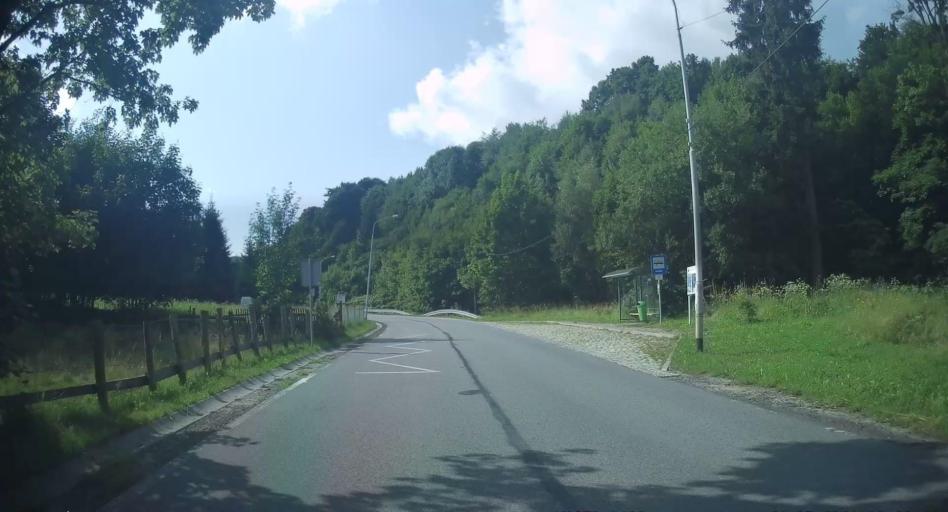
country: PL
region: Lower Silesian Voivodeship
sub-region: Powiat walbrzyski
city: Walim
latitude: 50.6815
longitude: 16.4394
